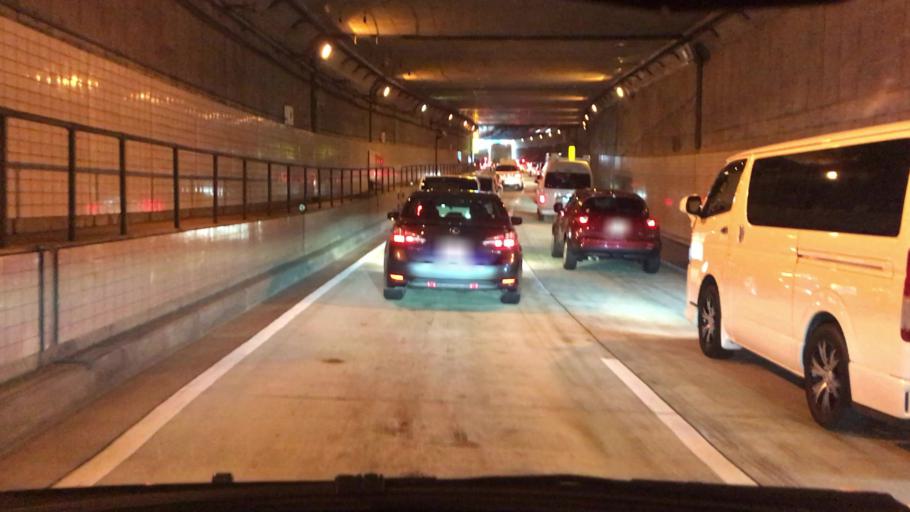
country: JP
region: Hyogo
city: Kobe
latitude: 34.7118
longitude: 135.1948
